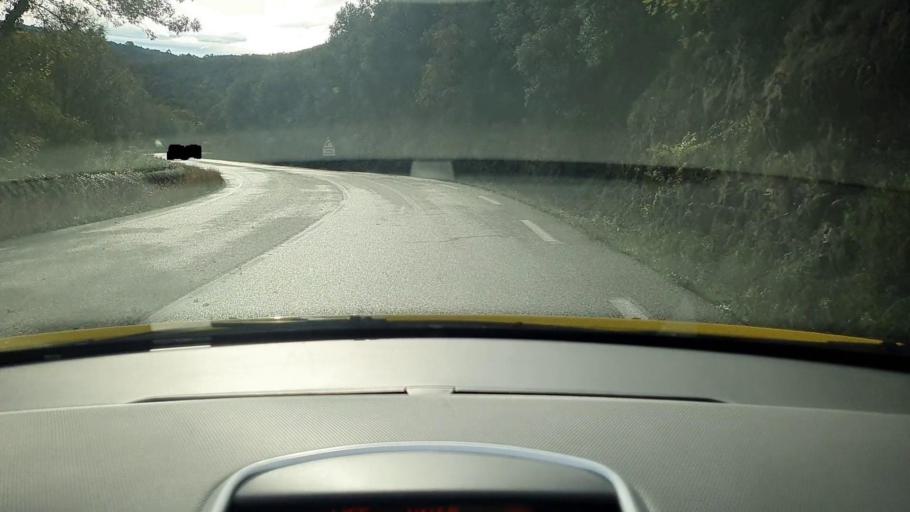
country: FR
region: Languedoc-Roussillon
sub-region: Departement du Gard
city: Anduze
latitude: 44.0692
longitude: 3.9349
